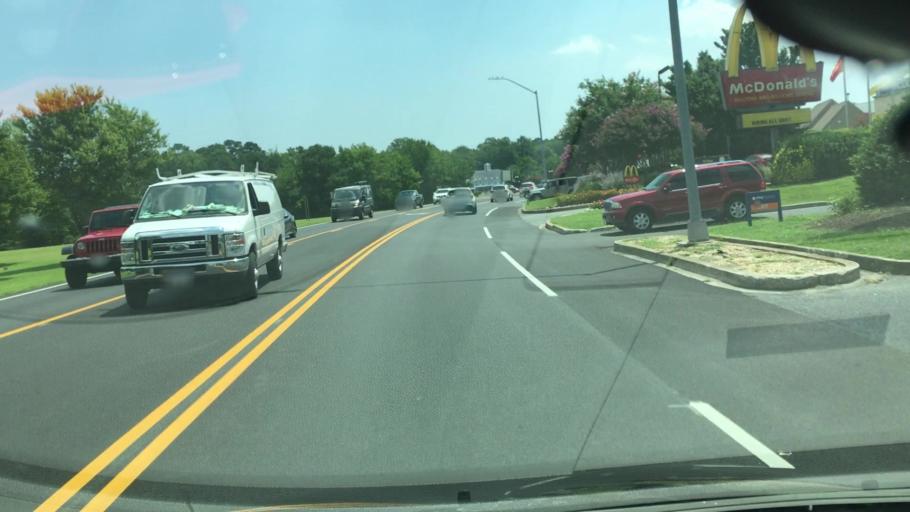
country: US
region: Maryland
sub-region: Worcester County
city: Ocean Pines
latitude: 38.3778
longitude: -75.1654
